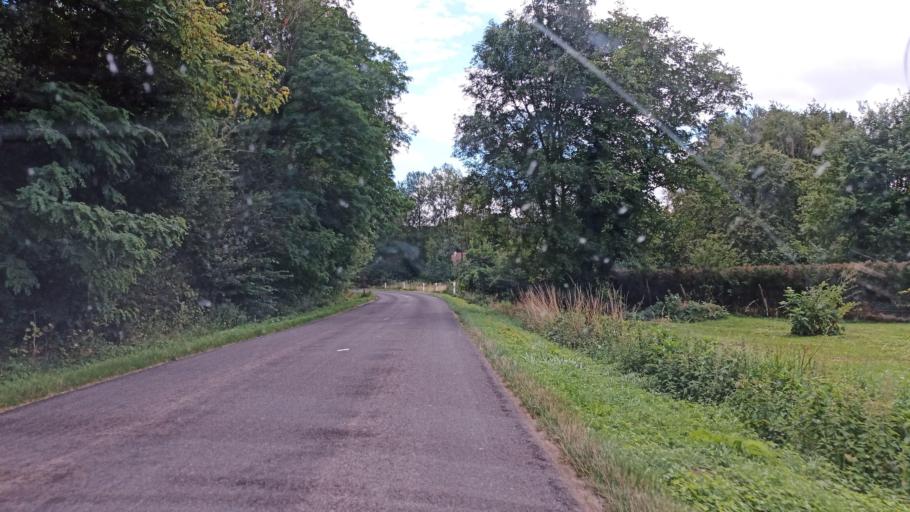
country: FR
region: Ile-de-France
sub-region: Departement de Seine-et-Marne
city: Voulx
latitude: 48.2559
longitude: 3.0178
